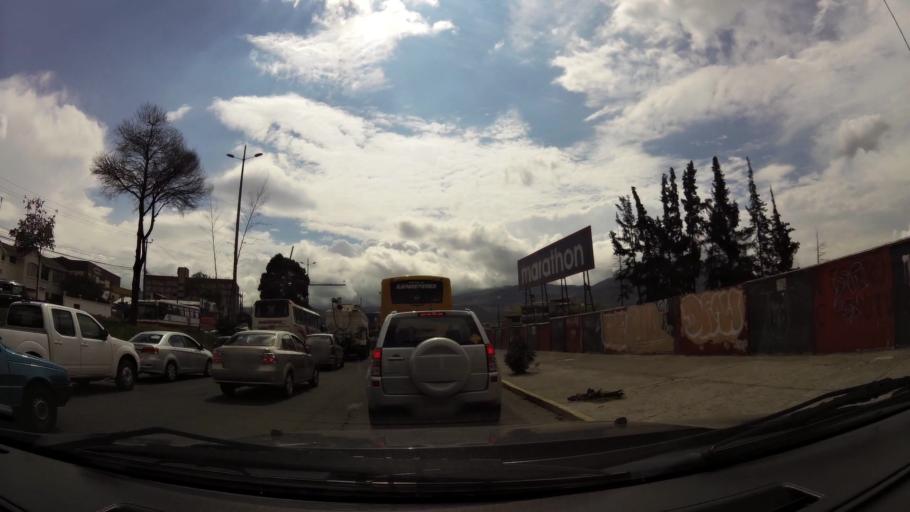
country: EC
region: Pichincha
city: Quito
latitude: -0.0922
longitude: -78.4718
